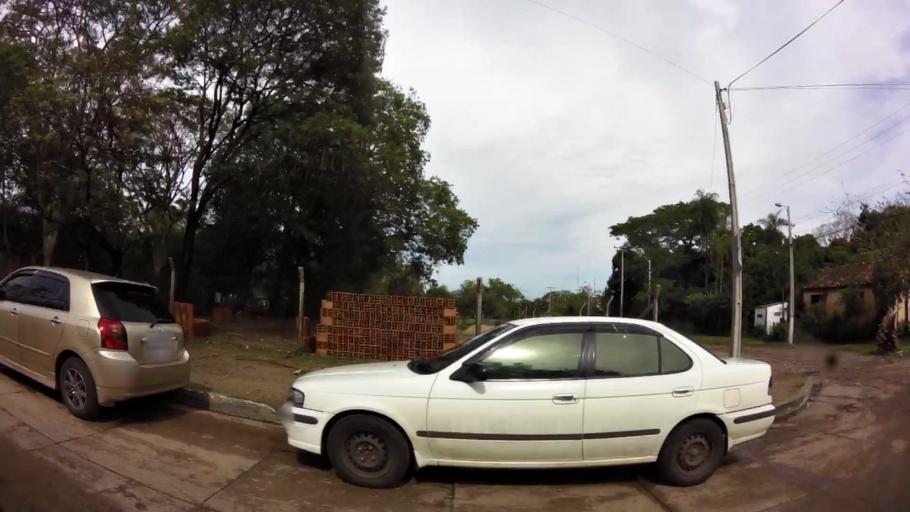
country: PY
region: Central
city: Limpio
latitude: -25.1638
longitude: -57.4762
